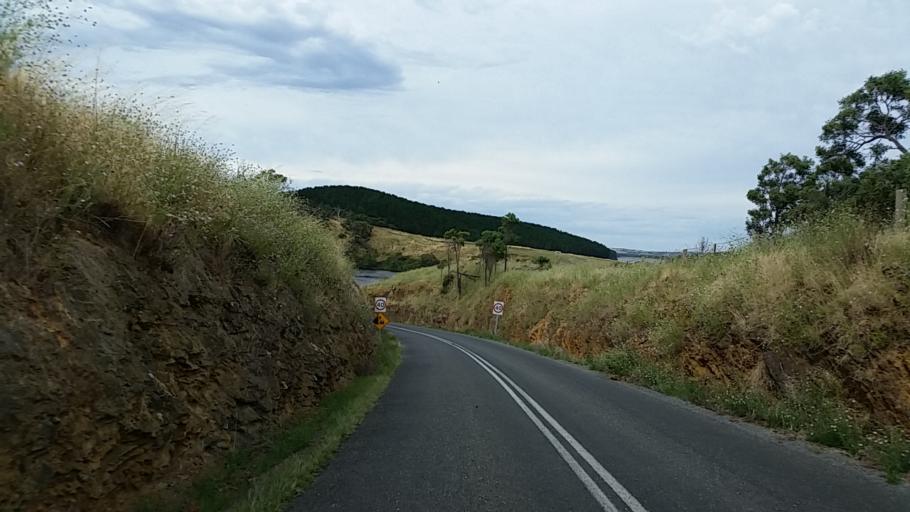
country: AU
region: South Australia
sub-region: Yankalilla
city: Normanville
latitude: -35.4027
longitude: 138.4184
